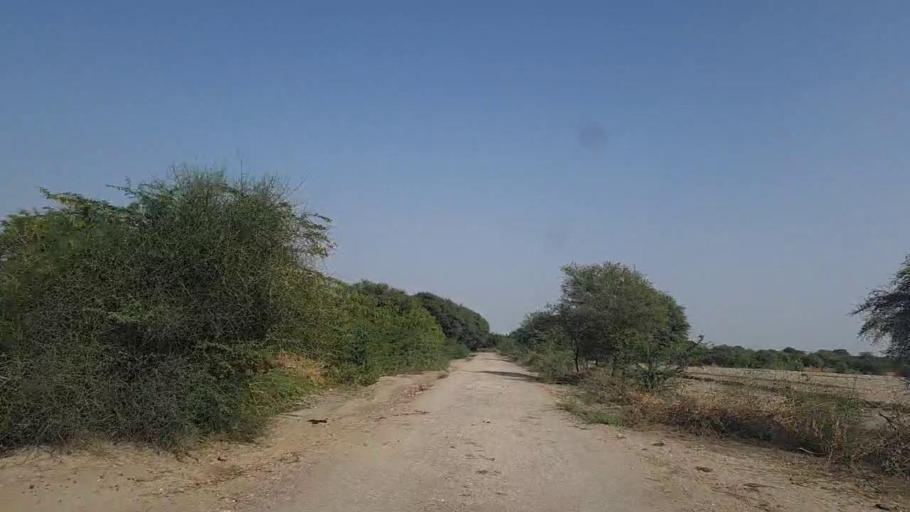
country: PK
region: Sindh
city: Naukot
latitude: 24.6096
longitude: 69.2826
